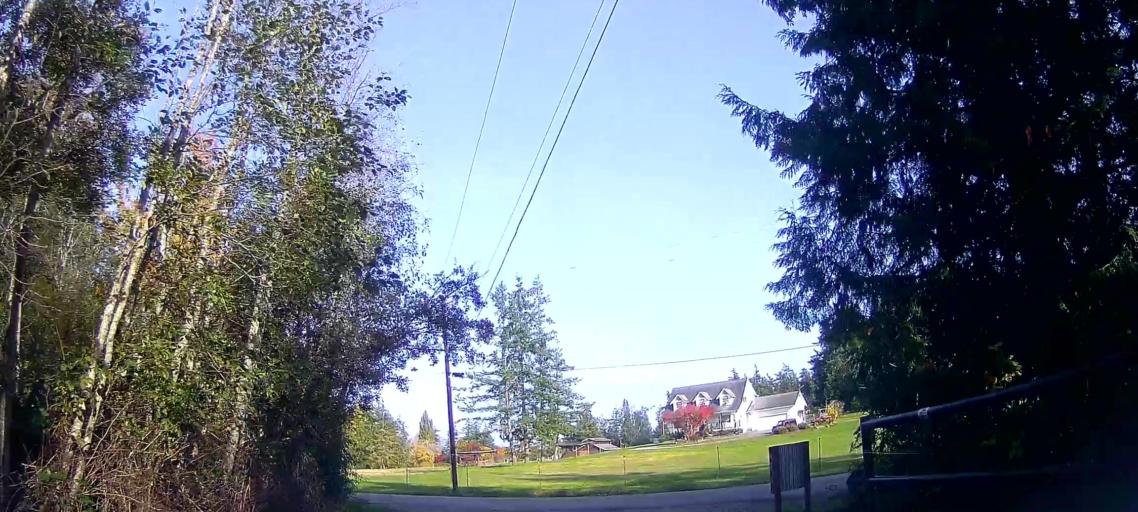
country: US
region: Washington
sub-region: Island County
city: Camano
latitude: 48.2008
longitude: -122.4567
